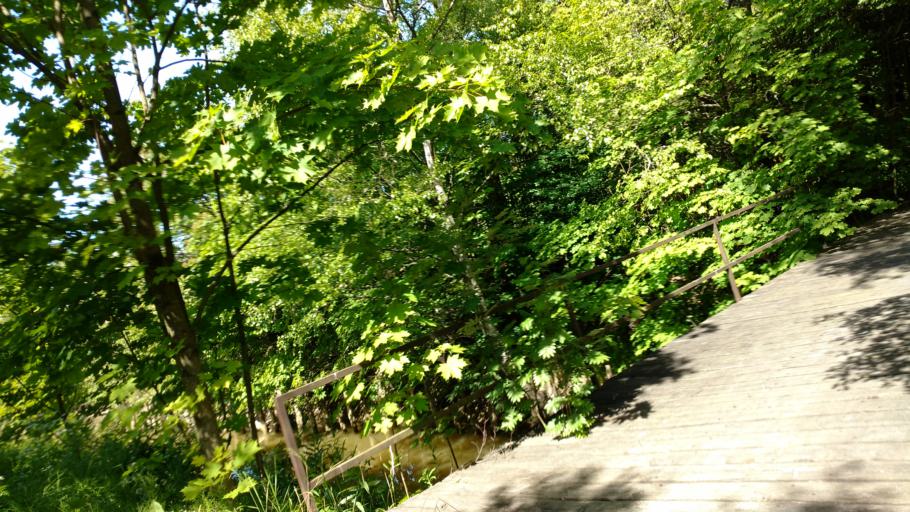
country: FI
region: Varsinais-Suomi
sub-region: Salo
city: Salo
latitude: 60.3794
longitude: 23.1189
